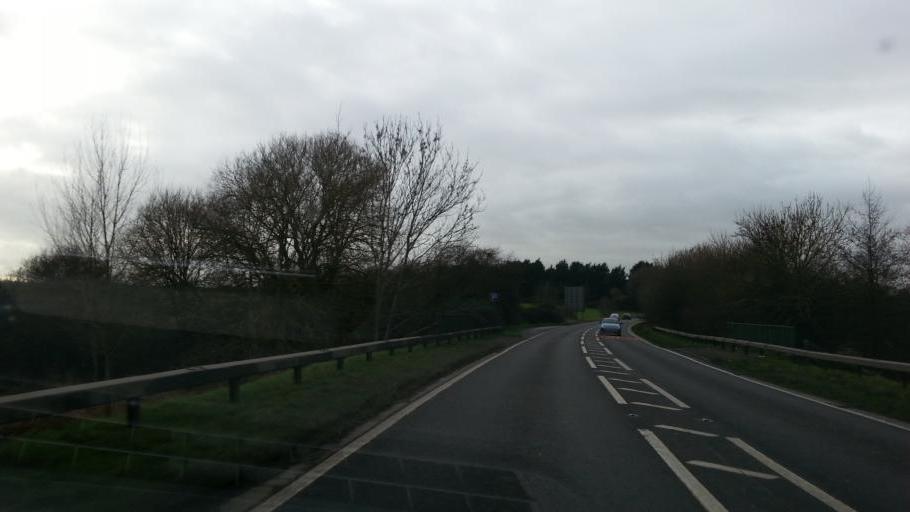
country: GB
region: England
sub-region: Cambridgeshire
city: Linton
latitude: 52.0931
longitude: 0.2932
